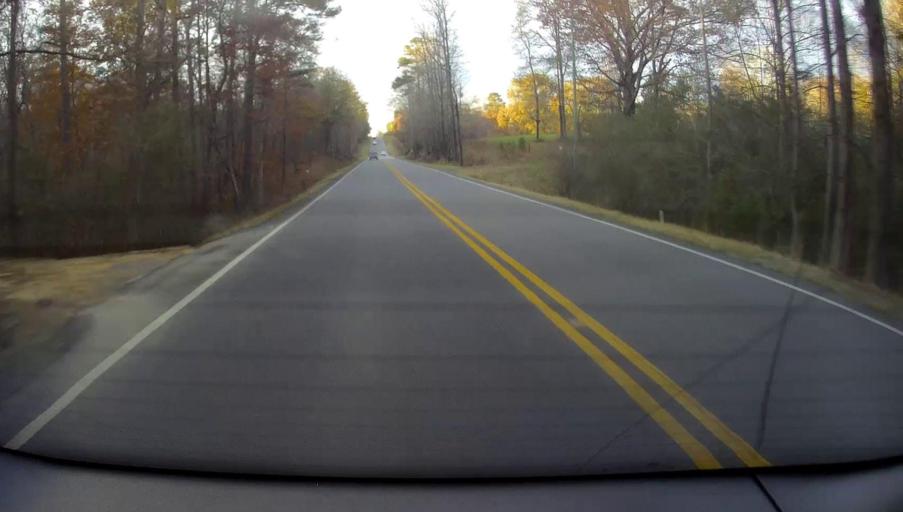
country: US
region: Alabama
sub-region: Blount County
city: Oneonta
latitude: 34.0858
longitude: -86.3468
